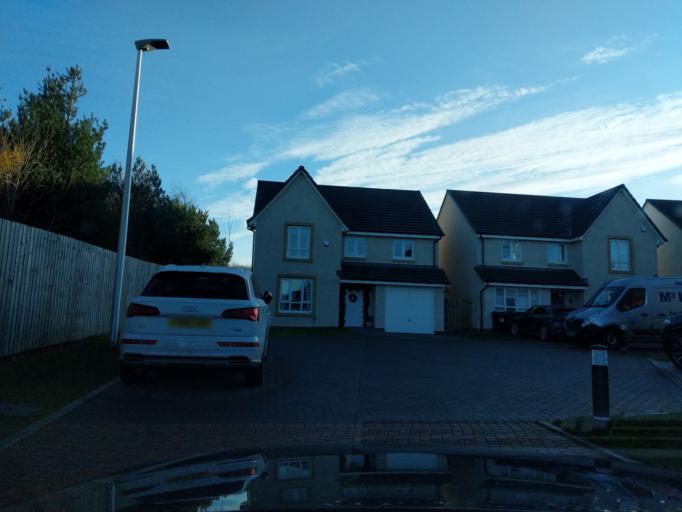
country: GB
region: Scotland
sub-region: Midlothian
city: Loanhead
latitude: 55.8949
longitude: -3.1519
